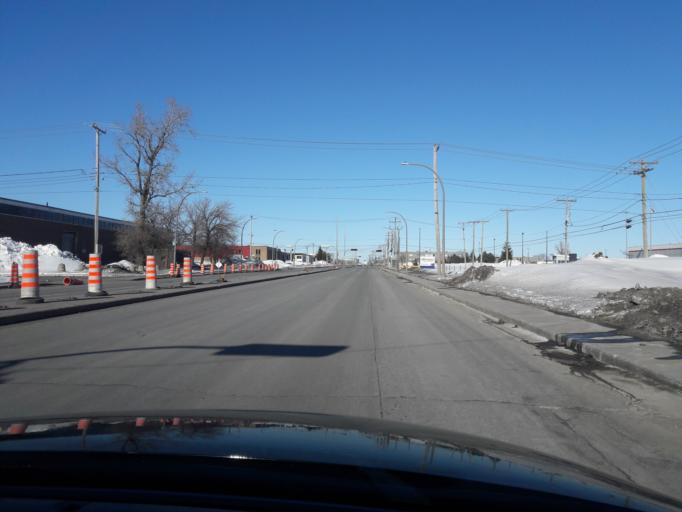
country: CA
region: Quebec
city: Dorval
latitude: 45.4826
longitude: -73.7226
